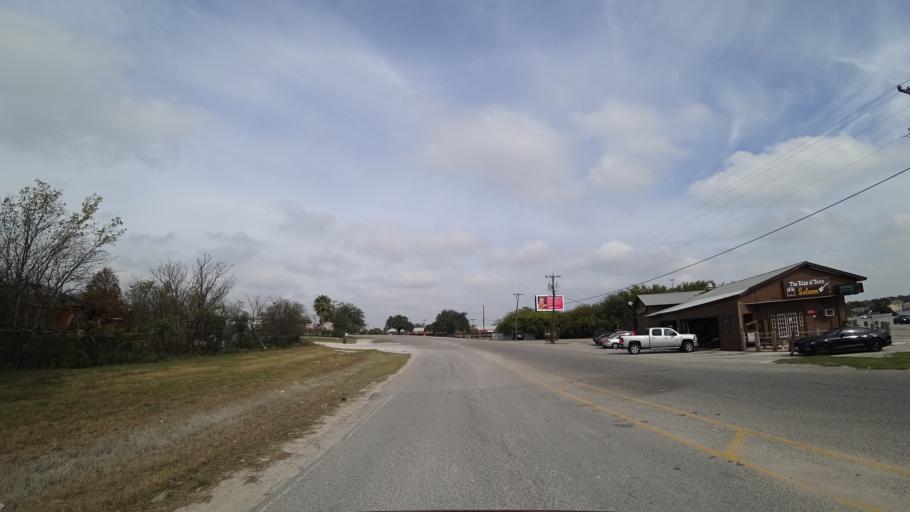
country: US
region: Texas
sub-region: Travis County
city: Windemere
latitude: 30.4490
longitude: -97.6617
